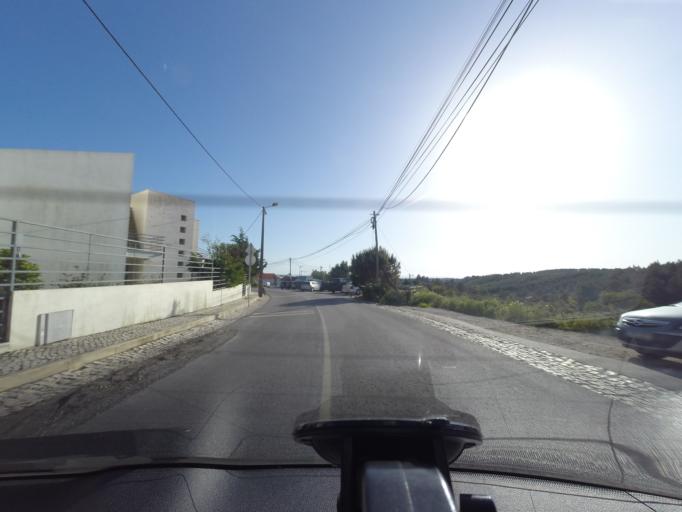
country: PT
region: Lisbon
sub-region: Cascais
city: Alcabideche
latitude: 38.7443
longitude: -9.4350
